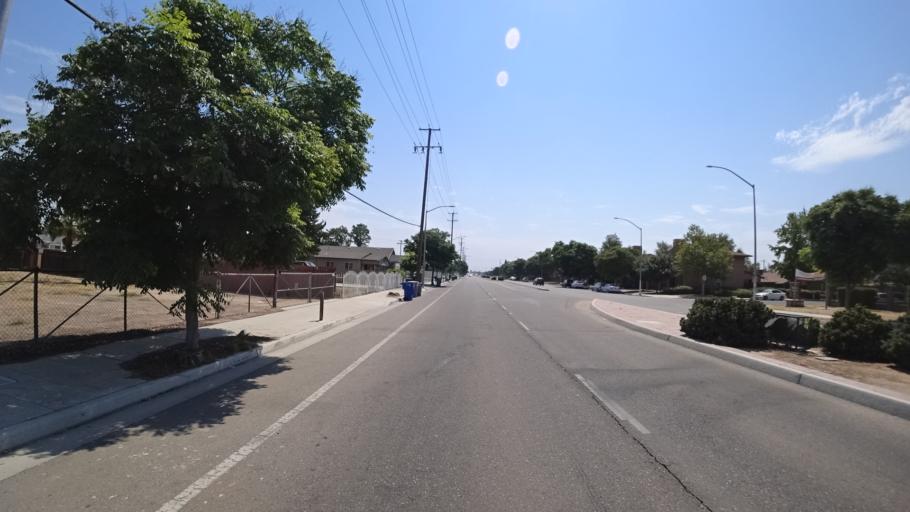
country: US
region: California
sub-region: Fresno County
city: West Park
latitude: 36.7214
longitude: -119.8236
